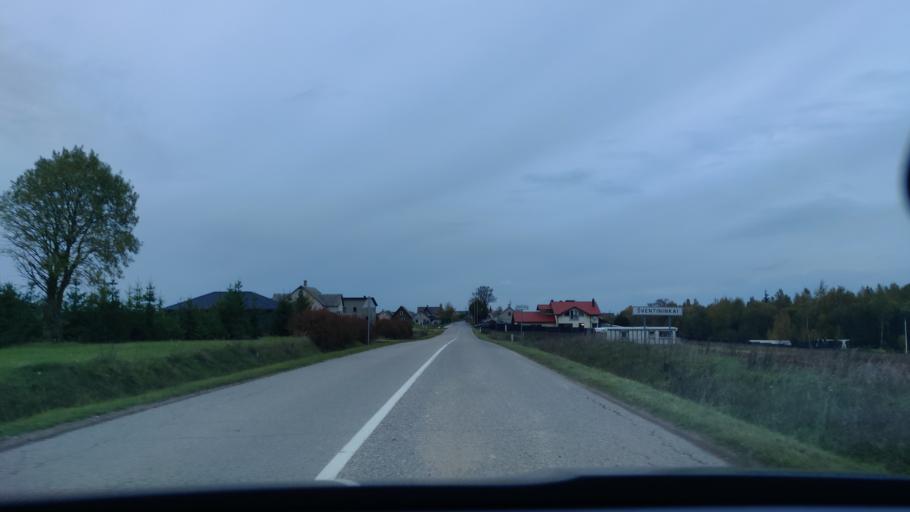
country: LT
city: Lentvaris
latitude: 54.5787
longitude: 25.0517
